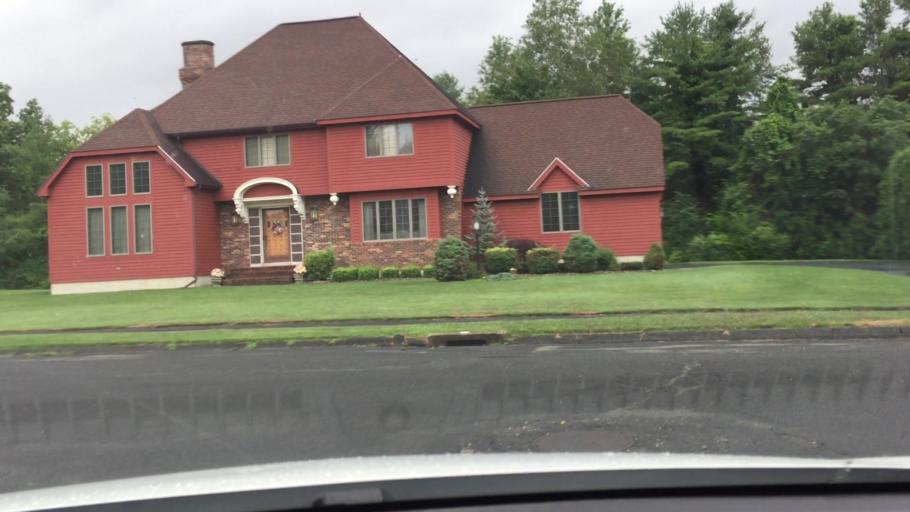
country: US
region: Massachusetts
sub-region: Berkshire County
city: Pittsfield
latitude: 42.4297
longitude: -73.2154
